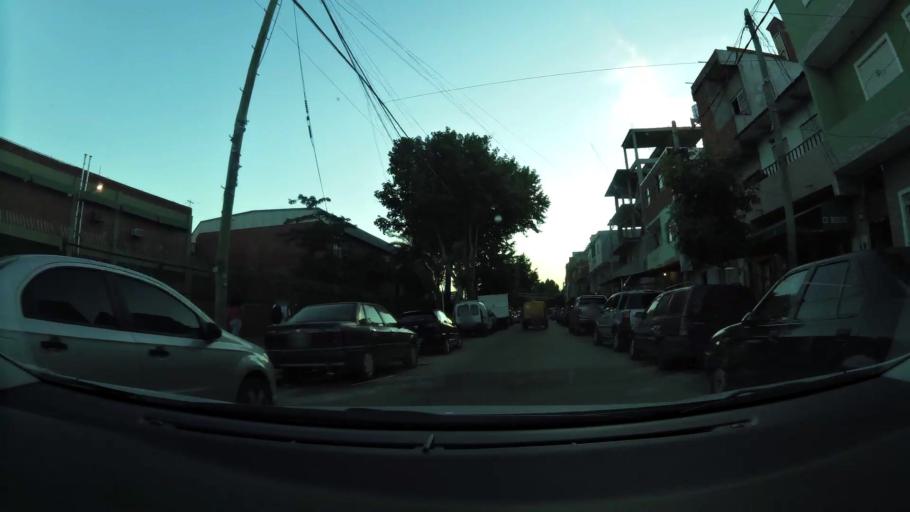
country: AR
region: Buenos Aires F.D.
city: Villa Lugano
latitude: -34.6788
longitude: -58.4671
